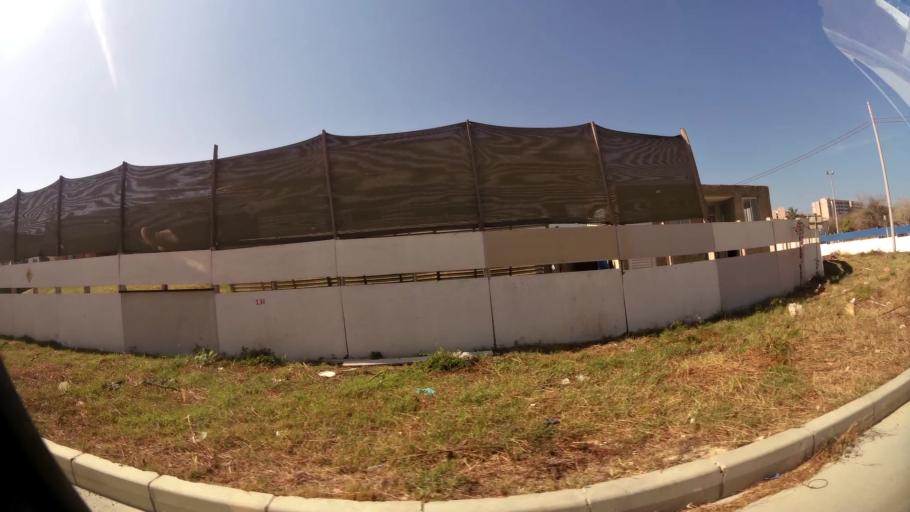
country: CO
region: Atlantico
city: Barranquilla
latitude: 11.0212
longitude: -74.8204
